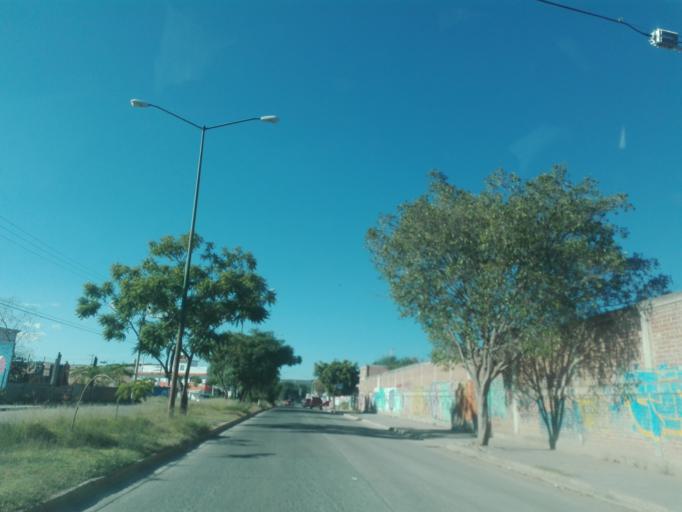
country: MX
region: Guanajuato
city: Leon
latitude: 21.1851
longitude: -101.6752
